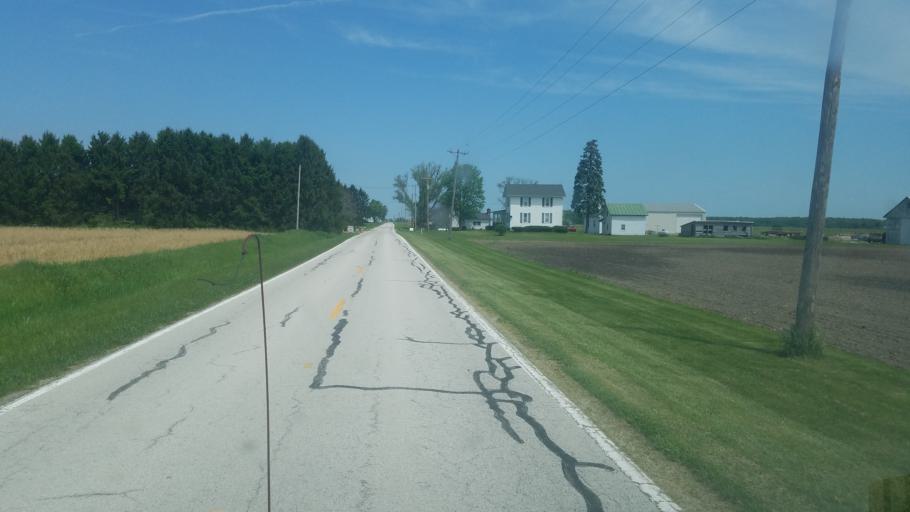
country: US
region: Ohio
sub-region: Ottawa County
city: Oak Harbor
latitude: 41.4449
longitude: -83.2016
